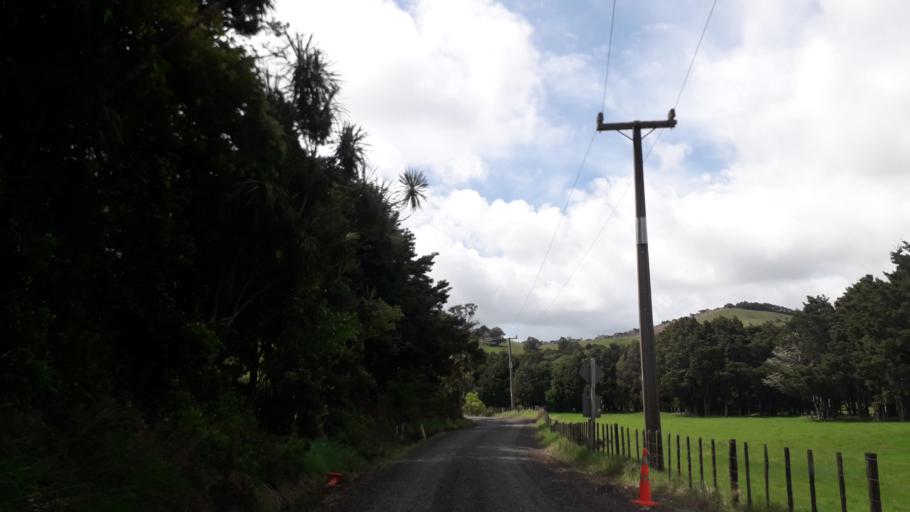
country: NZ
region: Northland
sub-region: Far North District
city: Ahipara
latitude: -35.2395
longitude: 173.2599
